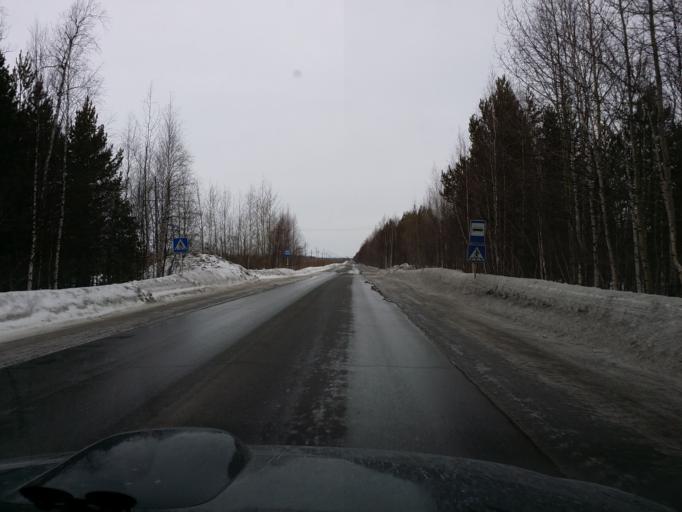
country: RU
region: Tomsk
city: Strezhevoy
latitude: 60.8009
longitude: 77.2953
